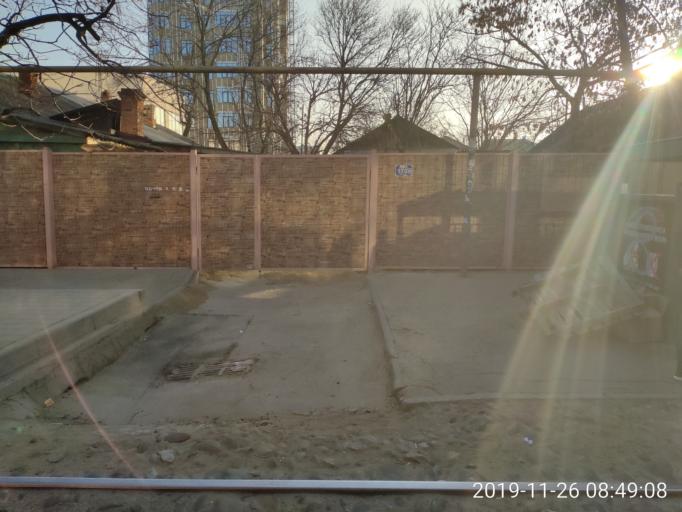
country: RU
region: Krasnodarskiy
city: Krasnodar
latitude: 45.0347
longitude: 38.9782
